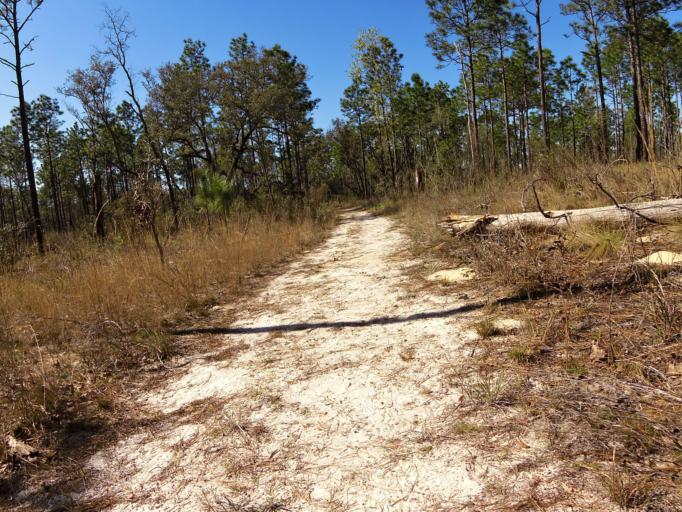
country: US
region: Florida
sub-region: Clay County
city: Keystone Heights
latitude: 29.8151
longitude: -82.0072
